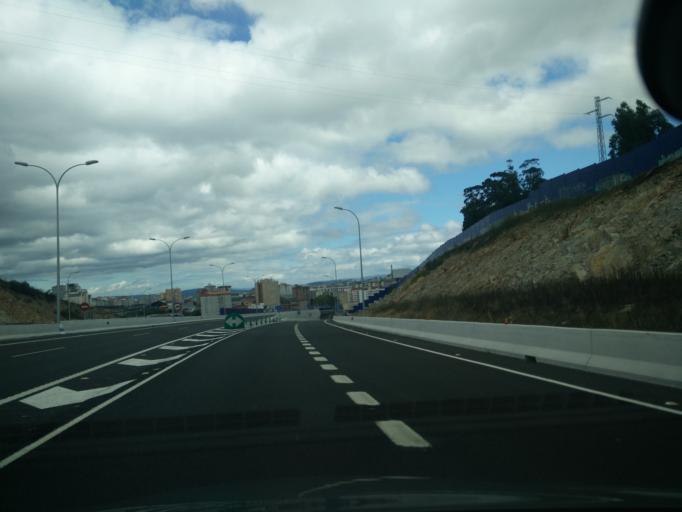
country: ES
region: Galicia
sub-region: Provincia da Coruna
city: A Coruna
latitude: 43.3422
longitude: -8.4213
